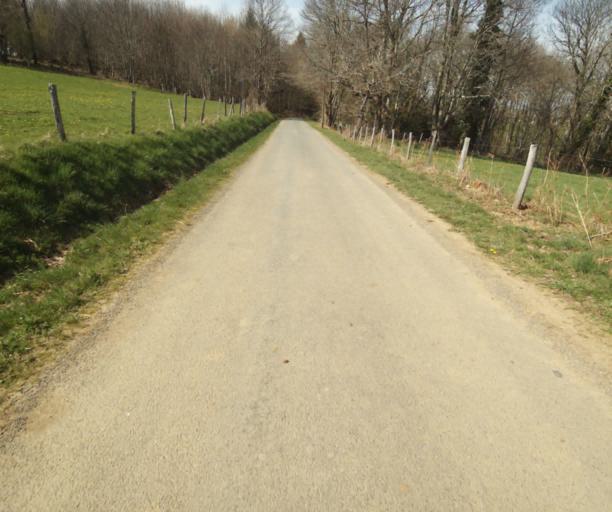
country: FR
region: Limousin
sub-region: Departement de la Correze
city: Naves
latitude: 45.3598
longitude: 1.7784
